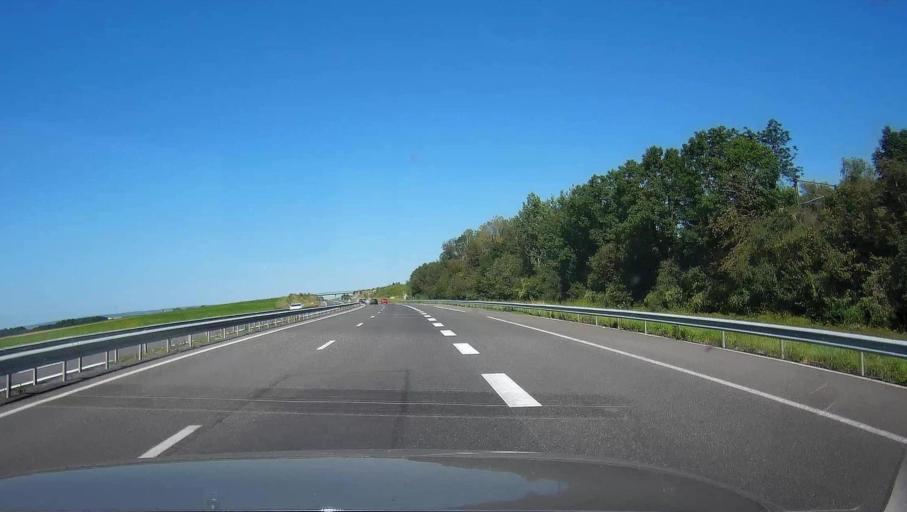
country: FR
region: Champagne-Ardenne
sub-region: Departement de la Marne
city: Fagnieres
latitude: 49.0105
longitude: 4.2979
